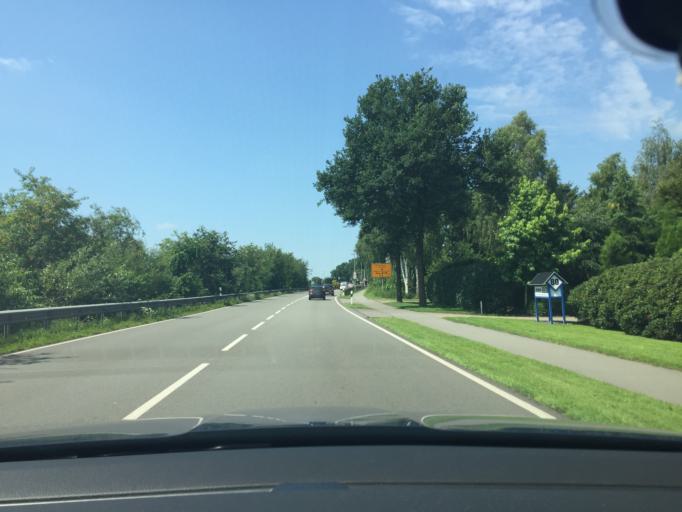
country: DE
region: Lower Saxony
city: Edewecht
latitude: 53.0900
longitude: 8.0599
